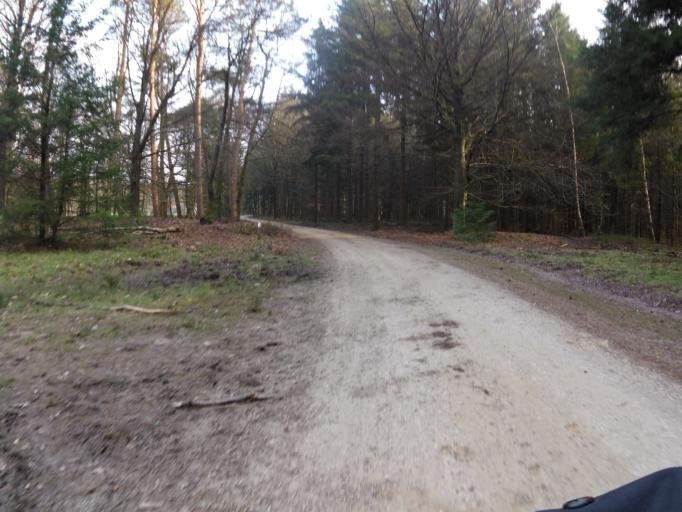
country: NL
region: Gelderland
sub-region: Gemeente Epe
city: Vaassen
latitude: 52.2547
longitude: 5.9167
